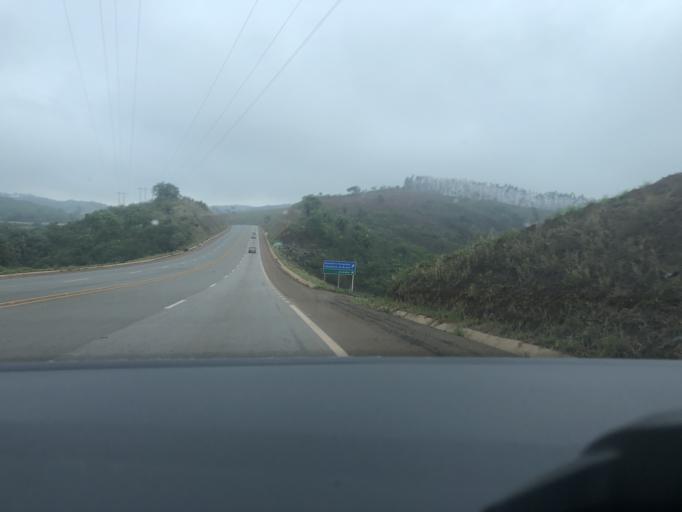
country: BR
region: Minas Gerais
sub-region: Congonhas
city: Congonhas
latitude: -20.6088
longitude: -43.9305
